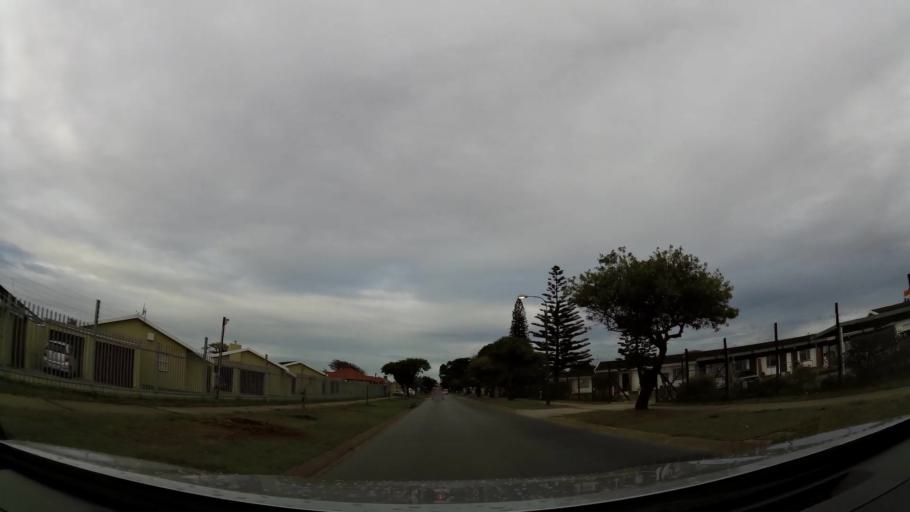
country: ZA
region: Eastern Cape
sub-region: Nelson Mandela Bay Metropolitan Municipality
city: Port Elizabeth
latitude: -33.9822
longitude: 25.5586
